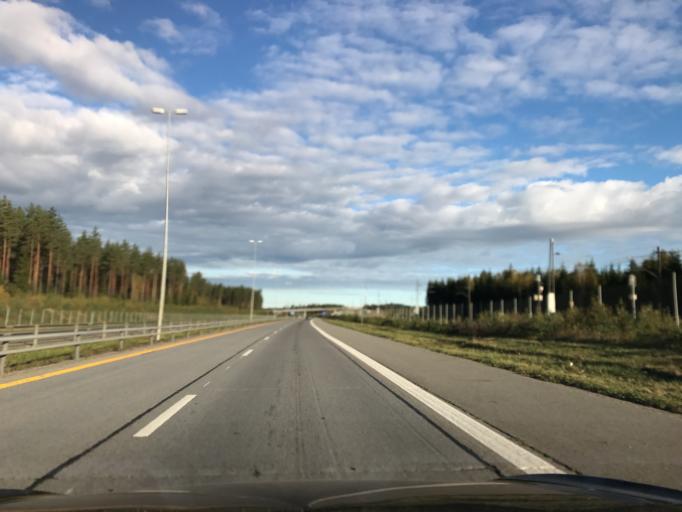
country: NO
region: Akershus
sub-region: Eidsvoll
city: Raholt
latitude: 60.2142
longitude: 11.1828
